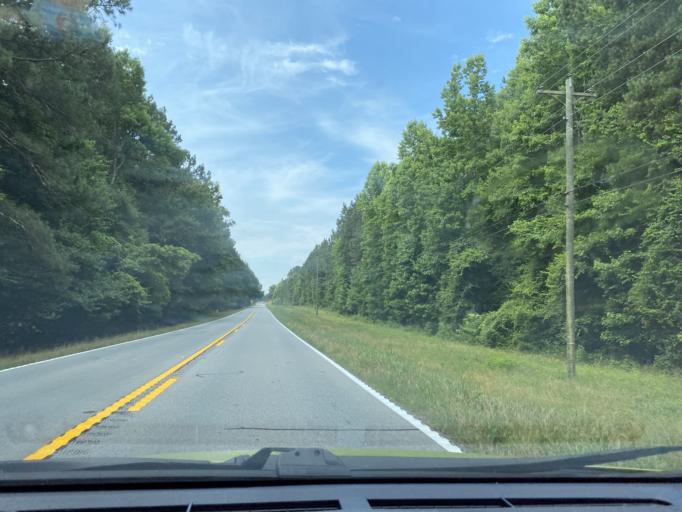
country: US
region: Georgia
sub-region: Coweta County
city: Senoia
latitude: 33.3092
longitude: -84.6546
